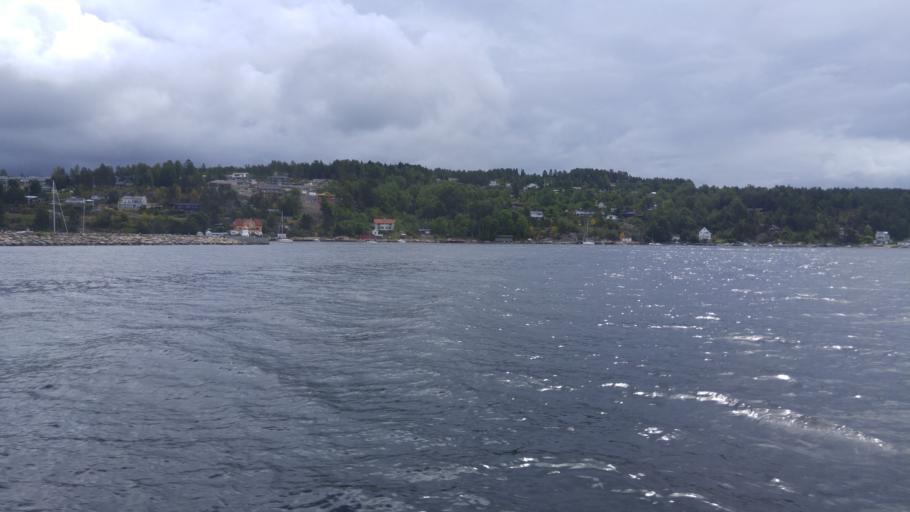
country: NO
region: Akershus
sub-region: Nesodden
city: Fagerstrand
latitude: 59.7318
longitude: 10.5839
